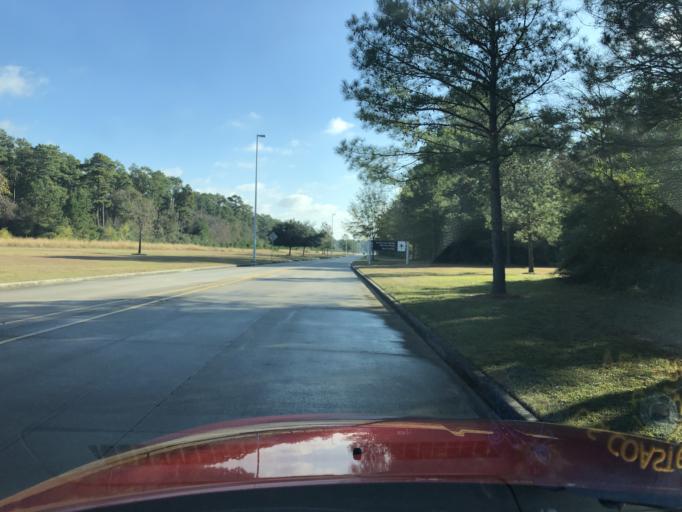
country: US
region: Texas
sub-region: Harris County
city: Aldine
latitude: 29.9726
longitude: -95.3344
